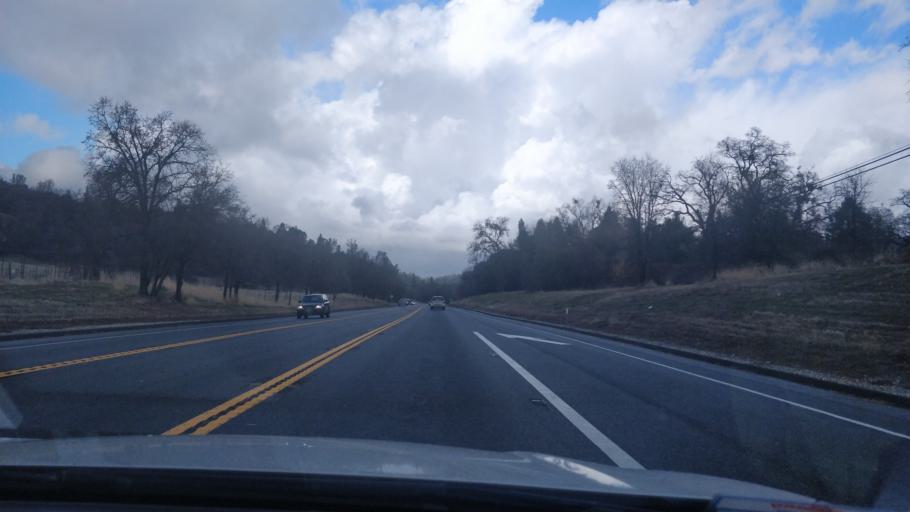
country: US
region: California
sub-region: Nevada County
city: Lake of the Pines
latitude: 39.0690
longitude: -121.0875
